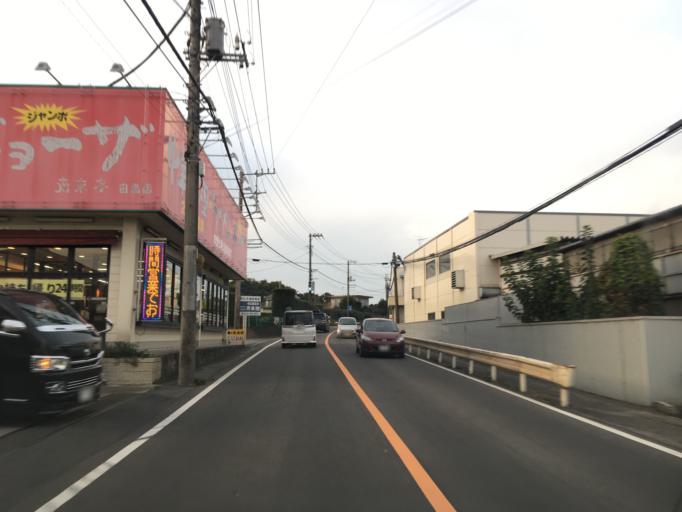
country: JP
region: Saitama
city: Sayama
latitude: 35.8817
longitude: 139.3776
